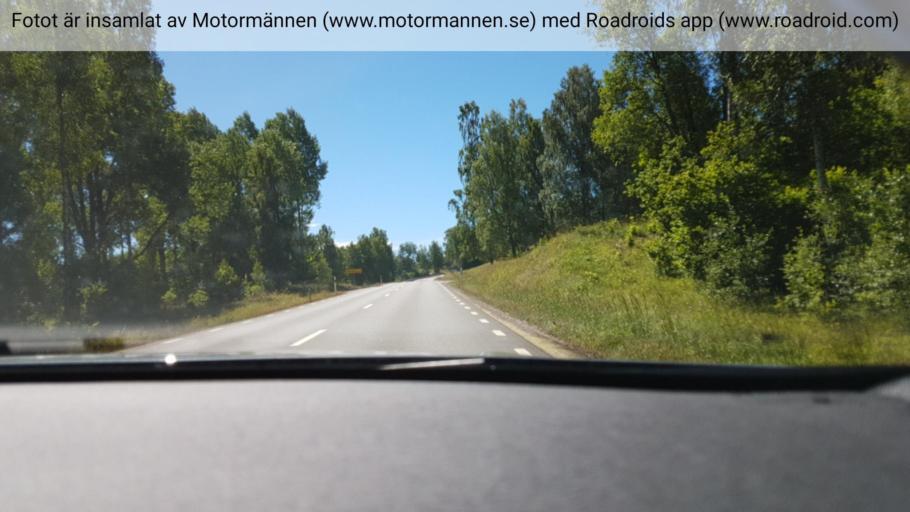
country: SE
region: Joenkoeping
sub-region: Mullsjo Kommun
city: Mullsjoe
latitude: 57.8602
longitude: 13.8578
